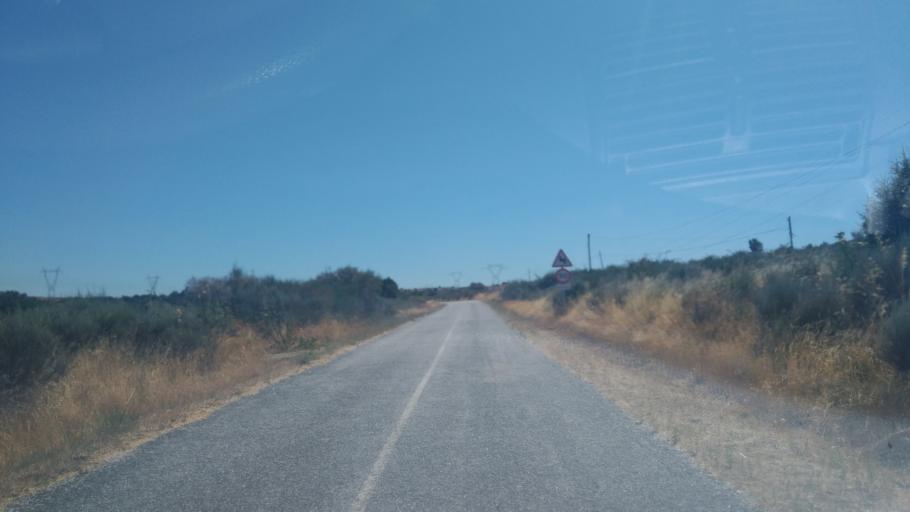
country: ES
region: Castille and Leon
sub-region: Provincia de Salamanca
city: Mieza
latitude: 41.2042
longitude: -6.6698
